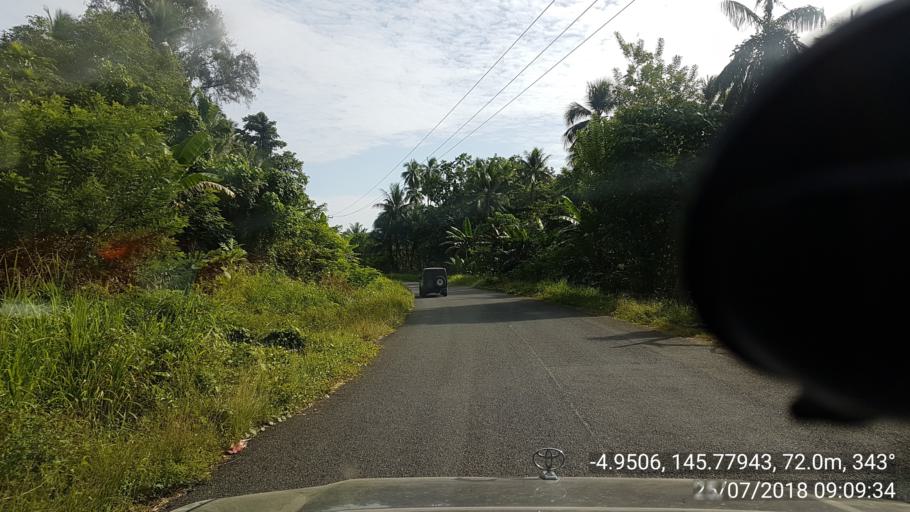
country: PG
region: Madang
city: Madang
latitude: -4.9508
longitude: 145.7794
